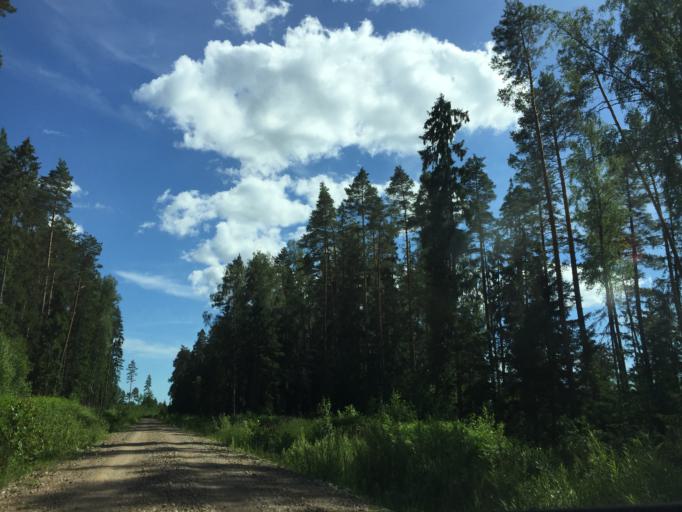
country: LV
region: Ventspils Rajons
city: Piltene
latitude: 57.0935
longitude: 21.8073
